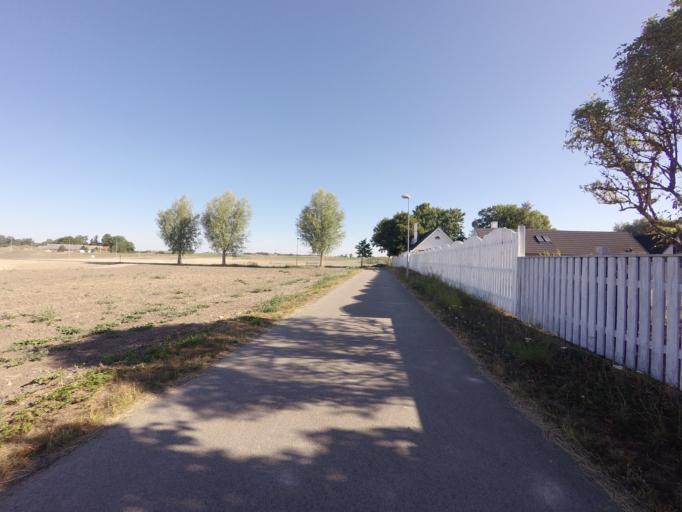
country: SE
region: Skane
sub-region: Trelleborgs Kommun
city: Skare
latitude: 55.4049
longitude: 13.0905
